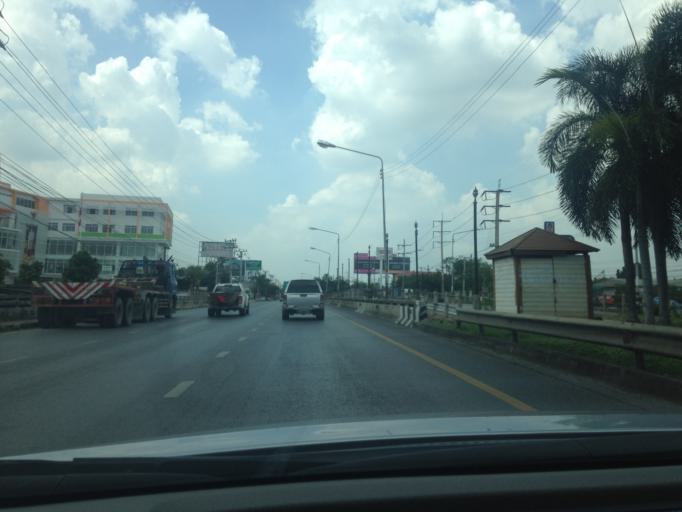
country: TH
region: Phra Nakhon Si Ayutthaya
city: Ban Bang Kadi Pathum Thani
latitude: 13.9943
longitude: 100.5774
